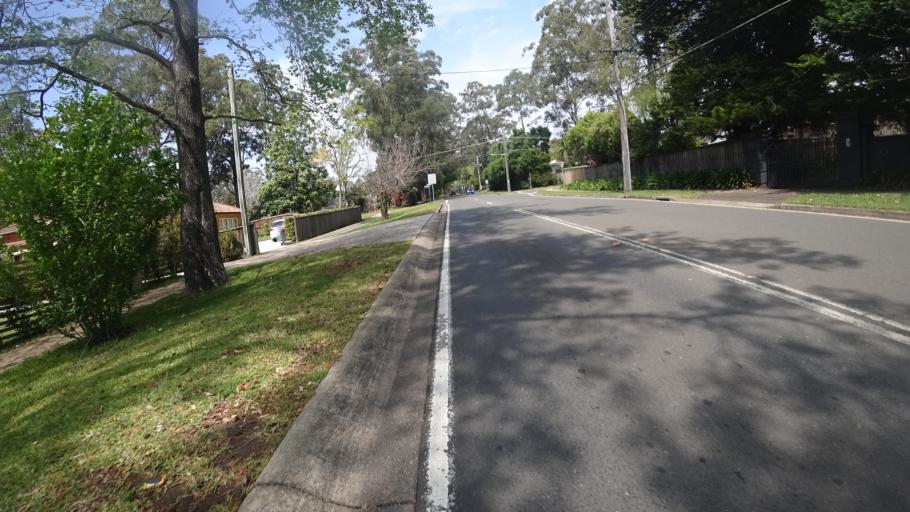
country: AU
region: New South Wales
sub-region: Ku-ring-gai
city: North Wahroonga
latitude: -33.7117
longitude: 151.1326
